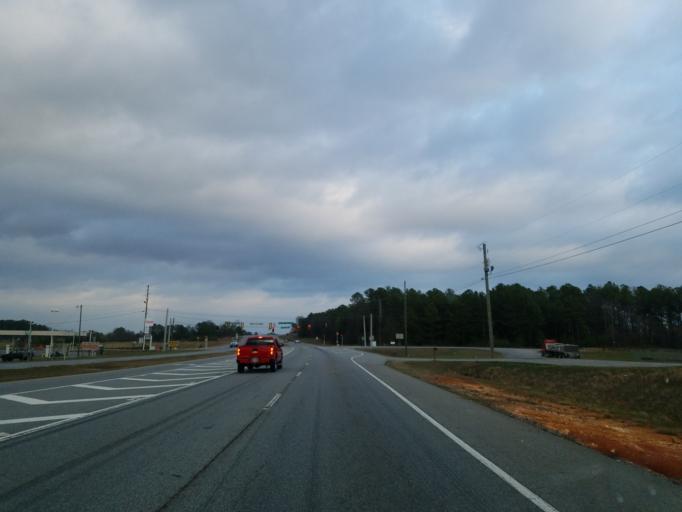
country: US
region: Georgia
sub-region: Bartow County
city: Euharlee
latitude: 34.1009
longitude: -84.9283
